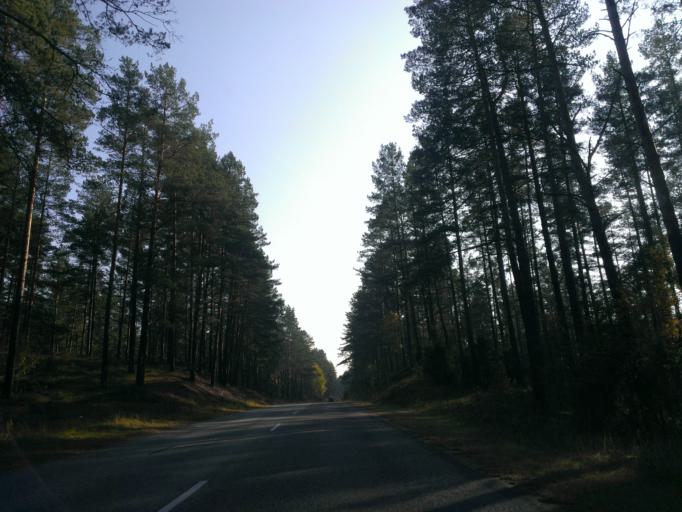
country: LV
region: Garkalne
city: Garkalne
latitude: 57.0269
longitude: 24.4299
